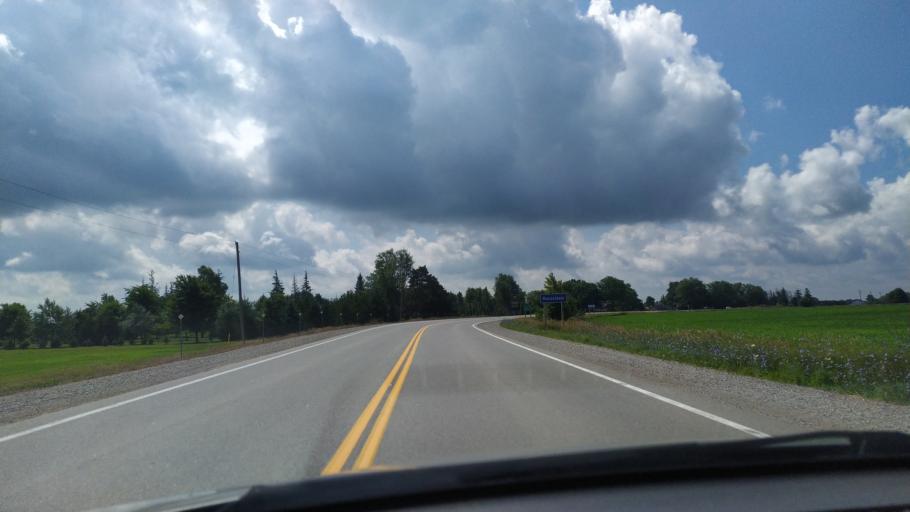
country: CA
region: Ontario
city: Huron East
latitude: 43.3897
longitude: -81.2596
